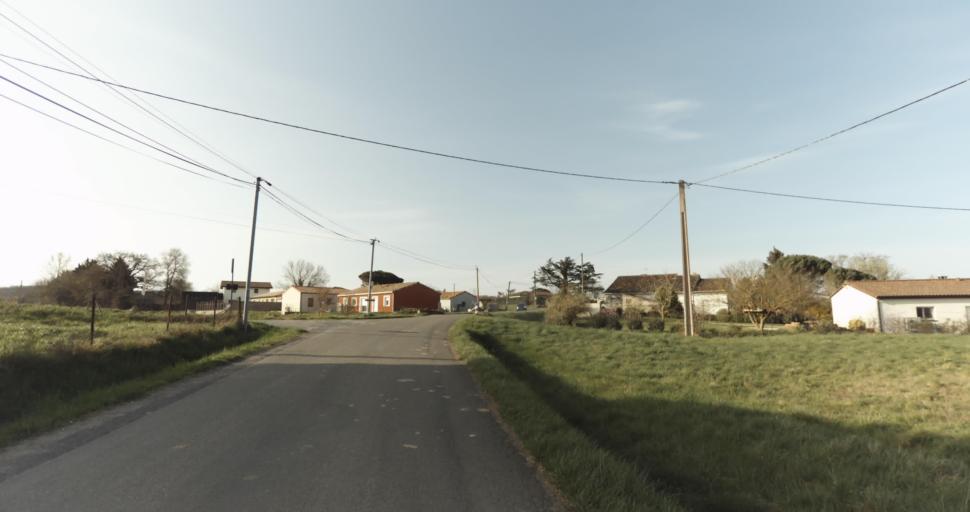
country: FR
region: Midi-Pyrenees
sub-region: Departement du Tarn
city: Saint-Sulpice-la-Pointe
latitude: 43.7592
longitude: 1.6779
